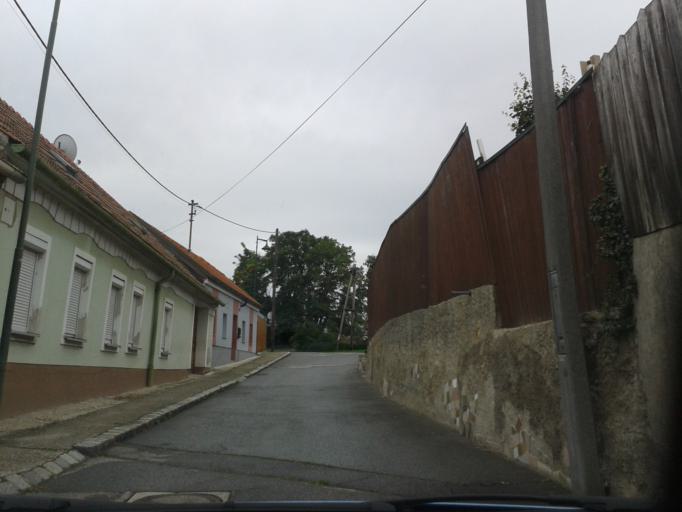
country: AT
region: Lower Austria
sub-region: Politischer Bezirk Ganserndorf
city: Drosing
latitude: 48.5590
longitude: 16.8759
